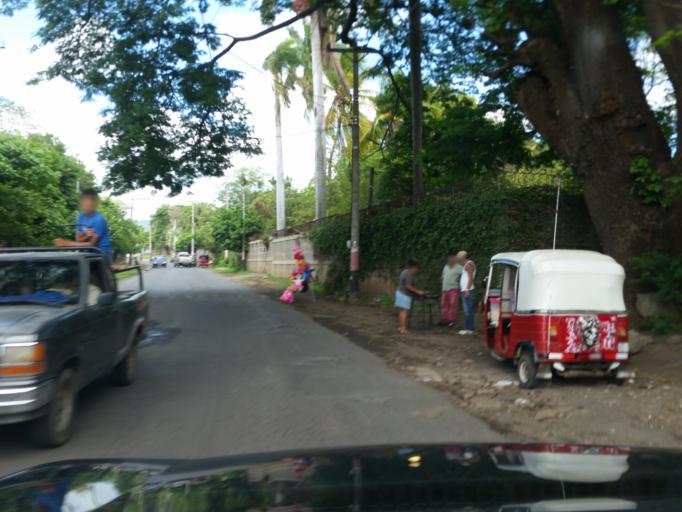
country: NI
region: Masaya
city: Ticuantepe
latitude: 12.0611
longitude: -86.1930
